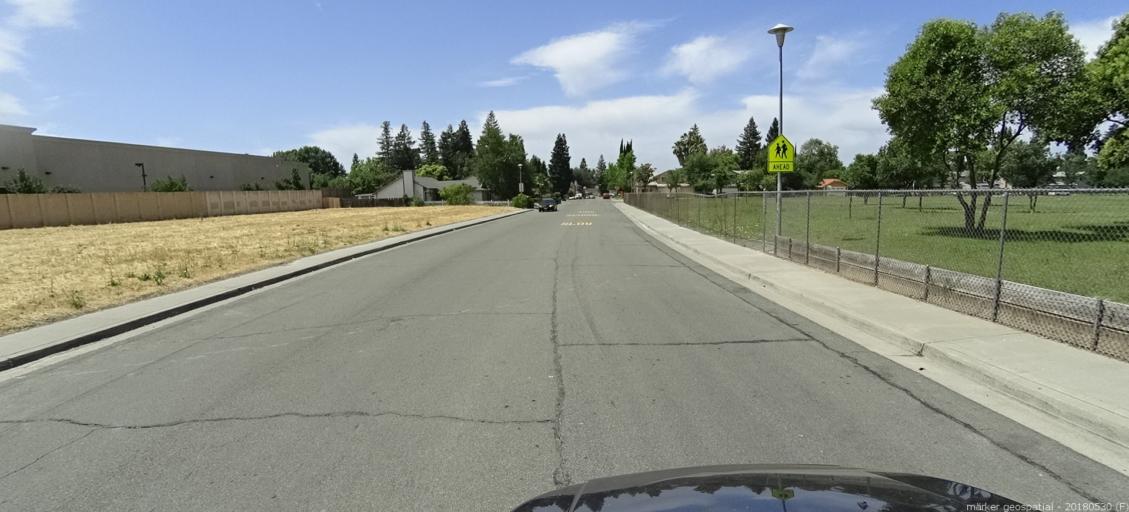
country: US
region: California
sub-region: Sacramento County
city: Sacramento
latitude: 38.6325
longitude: -121.4773
